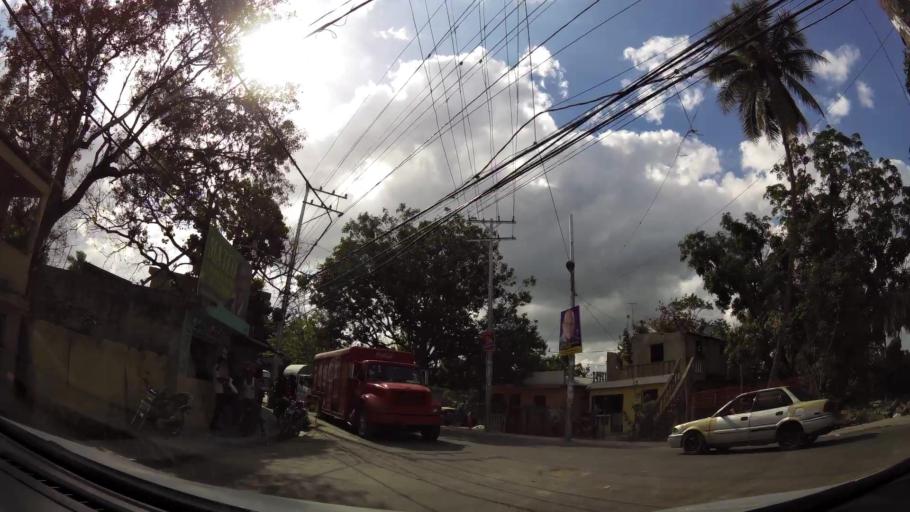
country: DO
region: Nacional
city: Ensanche Luperon
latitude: 18.5446
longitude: -69.8891
